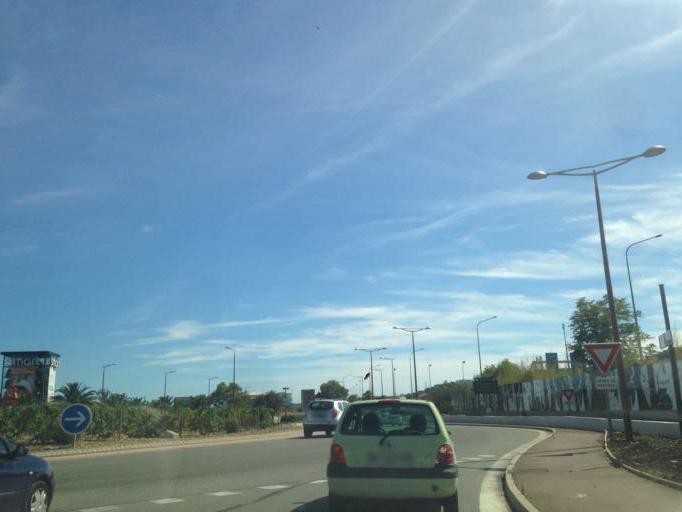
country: FR
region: Provence-Alpes-Cote d'Azur
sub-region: Departement des Alpes-Maritimes
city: Saint-Laurent-du-Var
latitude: 43.7030
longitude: 7.1890
